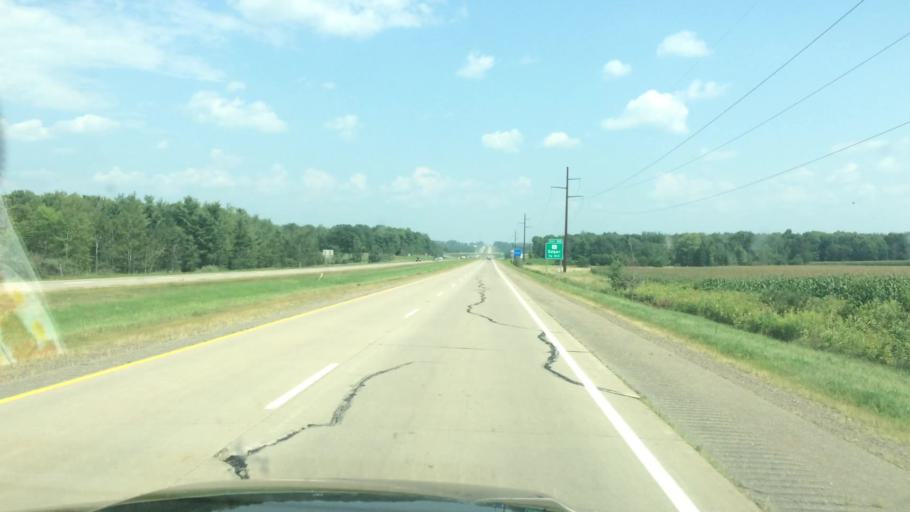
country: US
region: Wisconsin
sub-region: Marathon County
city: Edgar
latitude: 44.9442
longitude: -89.9821
